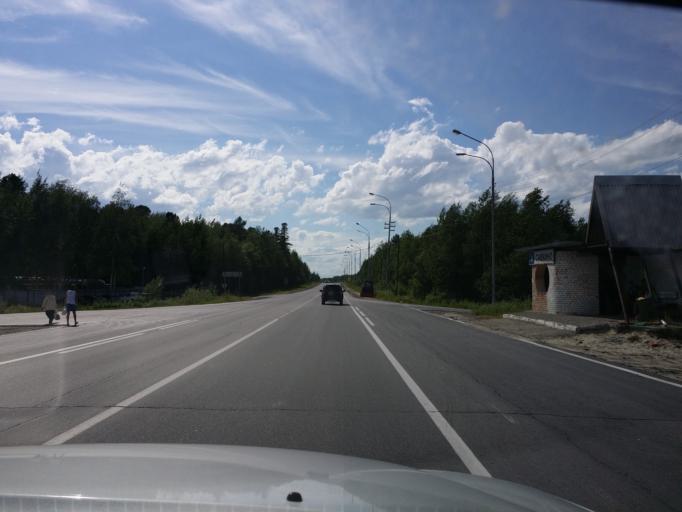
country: RU
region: Khanty-Mansiyskiy Avtonomnyy Okrug
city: Izluchinsk
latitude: 60.9651
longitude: 76.7907
